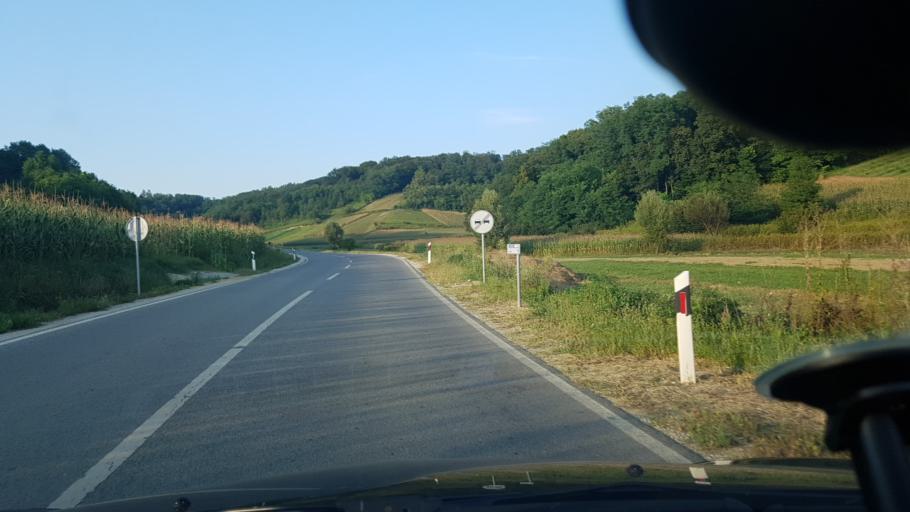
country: HR
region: Krapinsko-Zagorska
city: Pregrada
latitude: 46.1448
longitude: 15.7919
